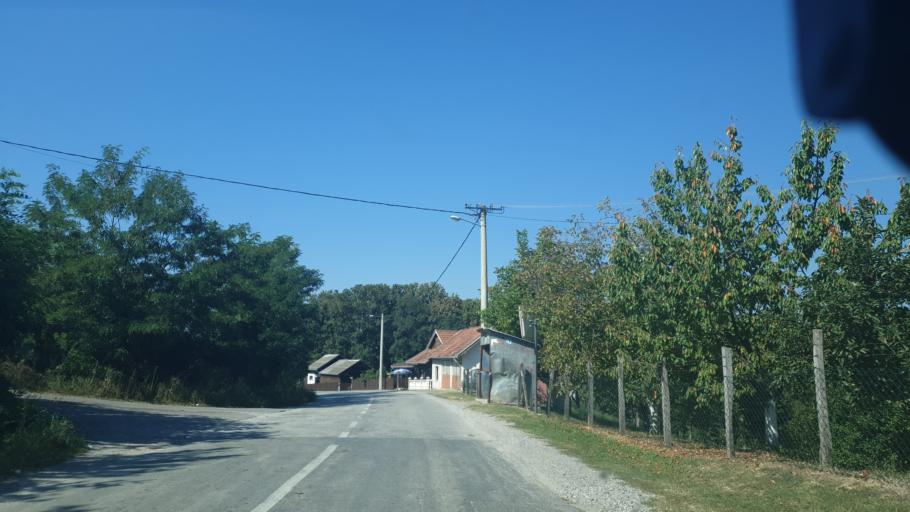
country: RS
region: Central Serbia
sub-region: Kolubarski Okrug
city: Lajkovac
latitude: 44.3090
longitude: 20.1610
